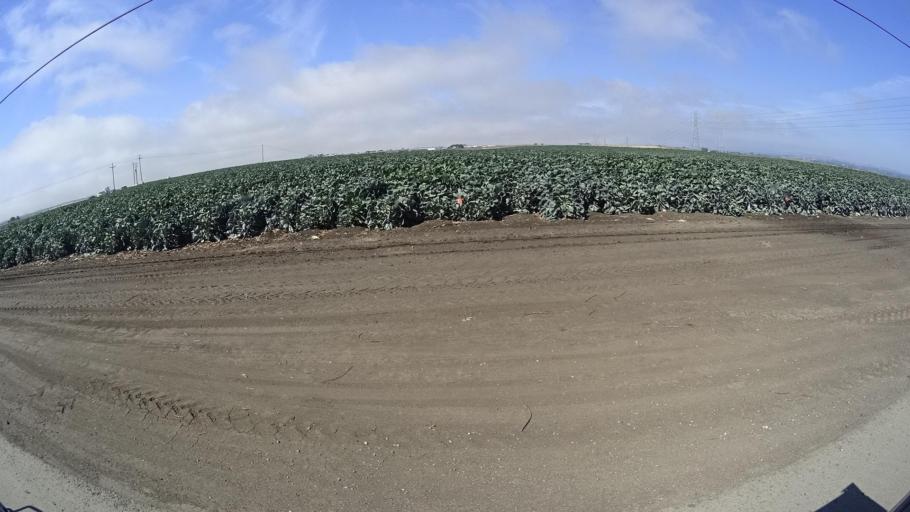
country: US
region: California
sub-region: Monterey County
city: Castroville
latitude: 36.7452
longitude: -121.7265
